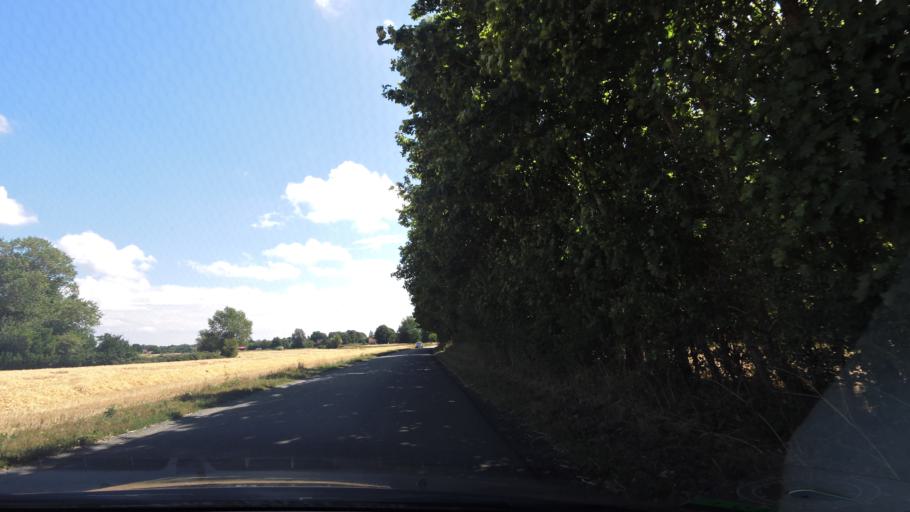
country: DK
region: South Denmark
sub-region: Nordfyns Kommune
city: Otterup
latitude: 55.5519
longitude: 10.4359
